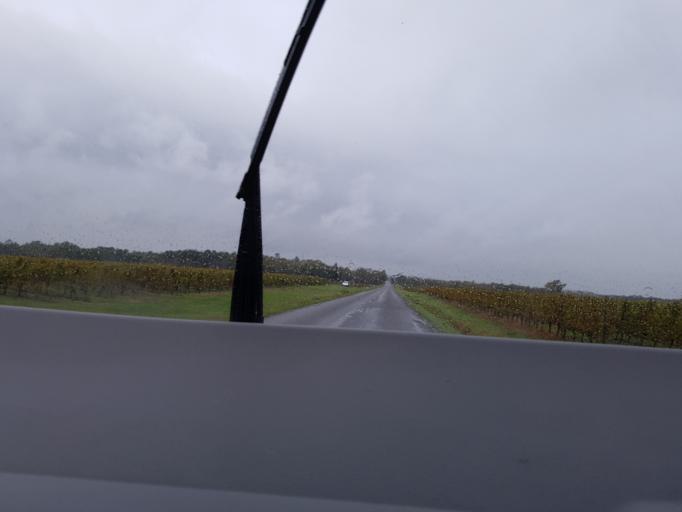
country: FR
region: Aquitaine
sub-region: Departement de la Gironde
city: Reignac
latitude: 45.2380
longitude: -0.5225
